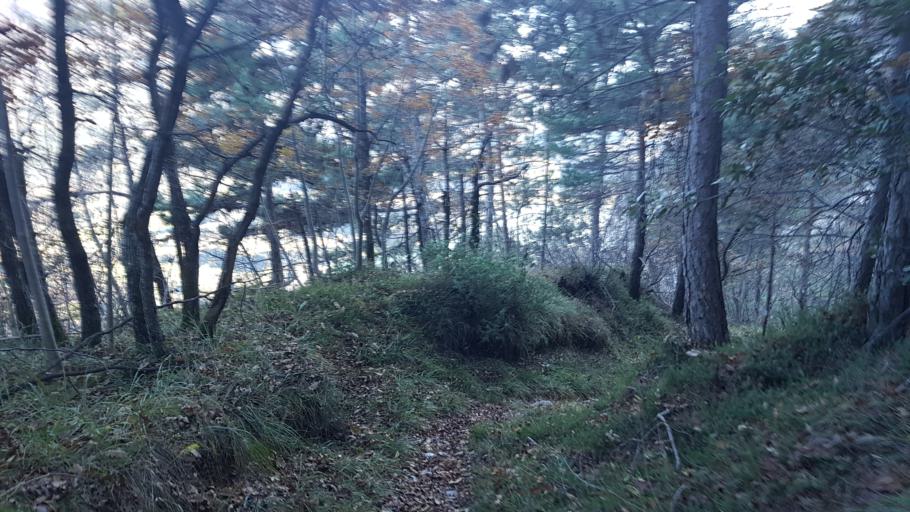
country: IT
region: Trentino-Alto Adige
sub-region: Provincia di Trento
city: Padergnone
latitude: 46.0761
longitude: 10.9798
